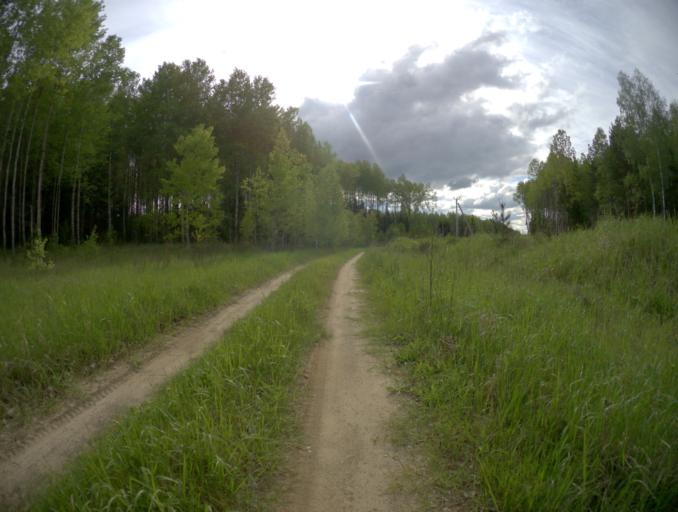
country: RU
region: Rjazan
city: Gus'-Zheleznyy
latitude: 55.1253
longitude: 41.1602
